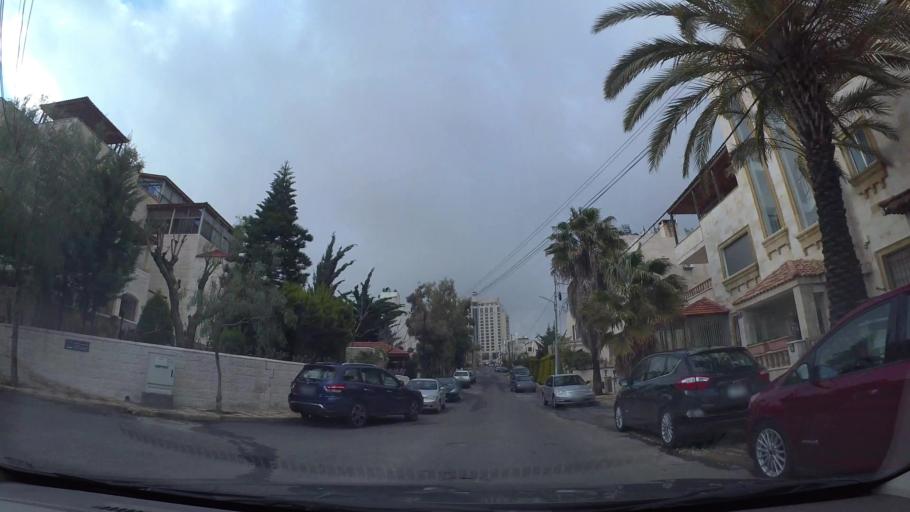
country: JO
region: Amman
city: Wadi as Sir
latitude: 31.9554
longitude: 35.8823
